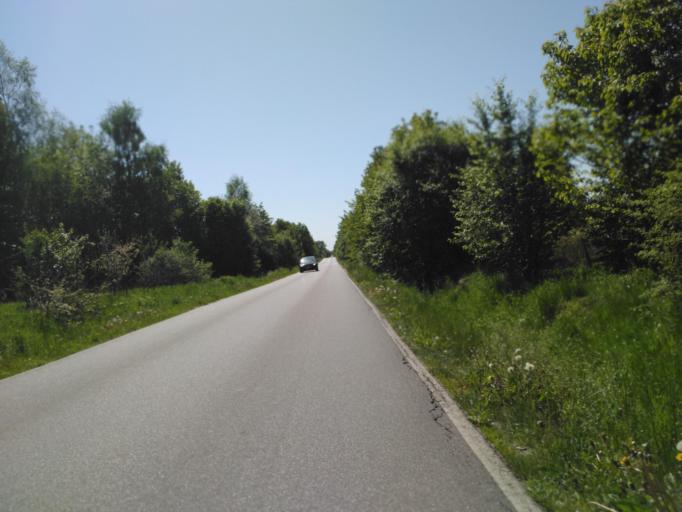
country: PL
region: Subcarpathian Voivodeship
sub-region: Krosno
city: Krosno
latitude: 49.6731
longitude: 21.7887
